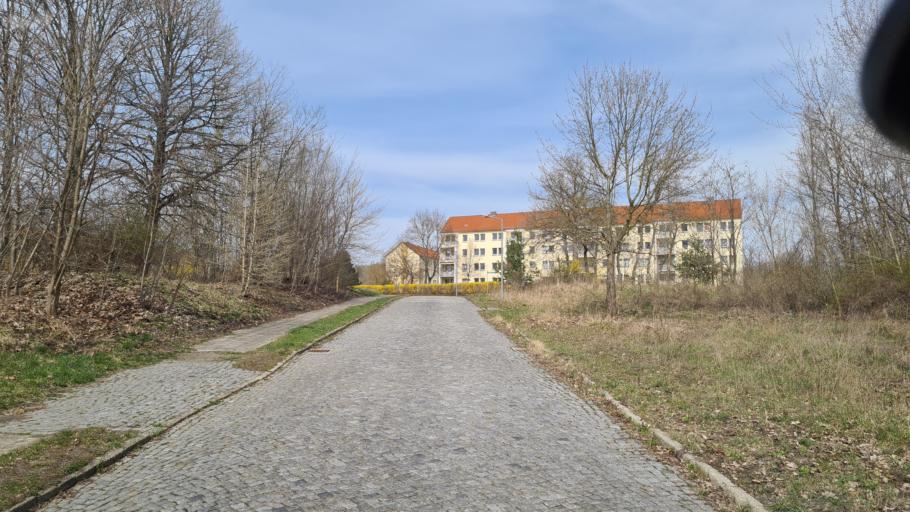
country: DE
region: Brandenburg
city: Lauchhammer
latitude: 51.4977
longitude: 13.7753
